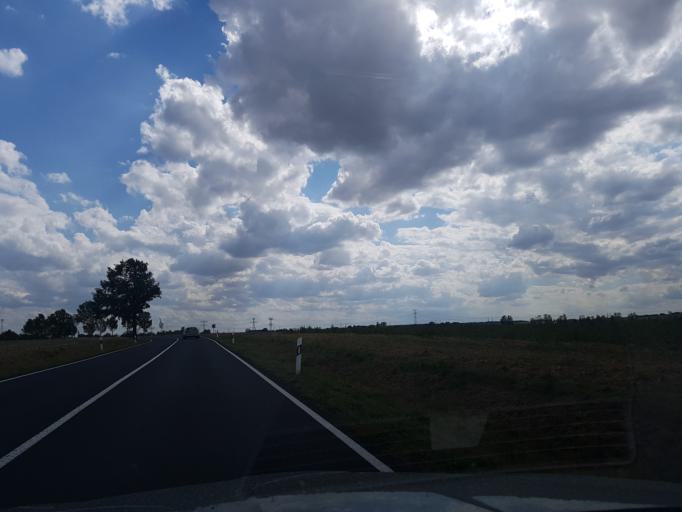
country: DE
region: Saxony
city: Priestewitz
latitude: 51.2471
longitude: 13.5477
